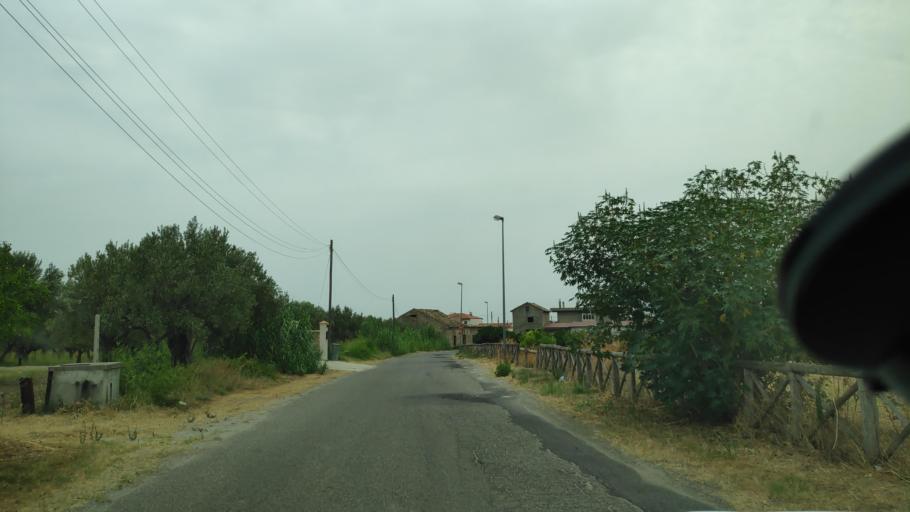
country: IT
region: Calabria
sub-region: Provincia di Catanzaro
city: Marina di Davoli
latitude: 38.6624
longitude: 16.5361
